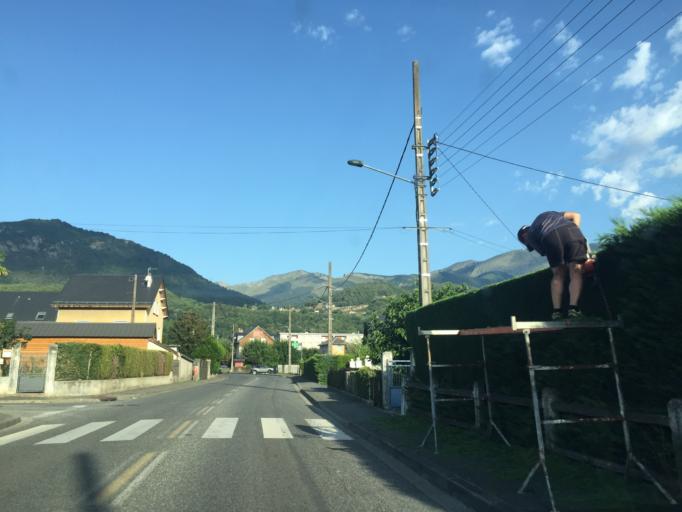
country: FR
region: Midi-Pyrenees
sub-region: Departement des Hautes-Pyrenees
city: Argeles-Gazost
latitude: 43.0059
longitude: -0.0889
